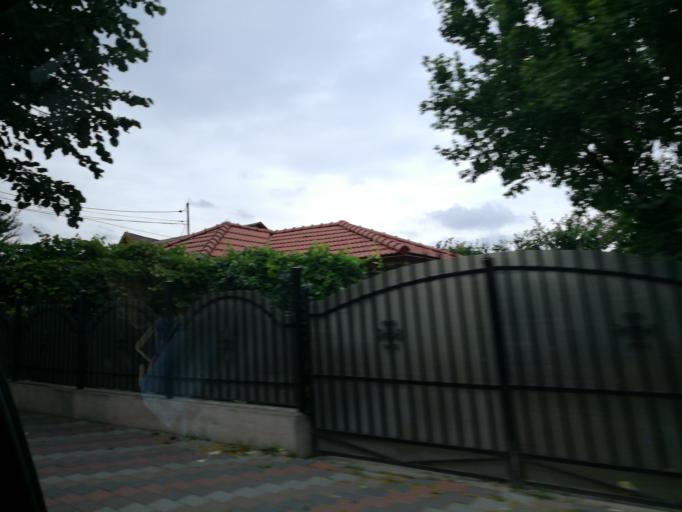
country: RO
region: Constanta
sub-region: Municipiul Mangalia
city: Mangalia
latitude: 43.8181
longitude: 28.5763
